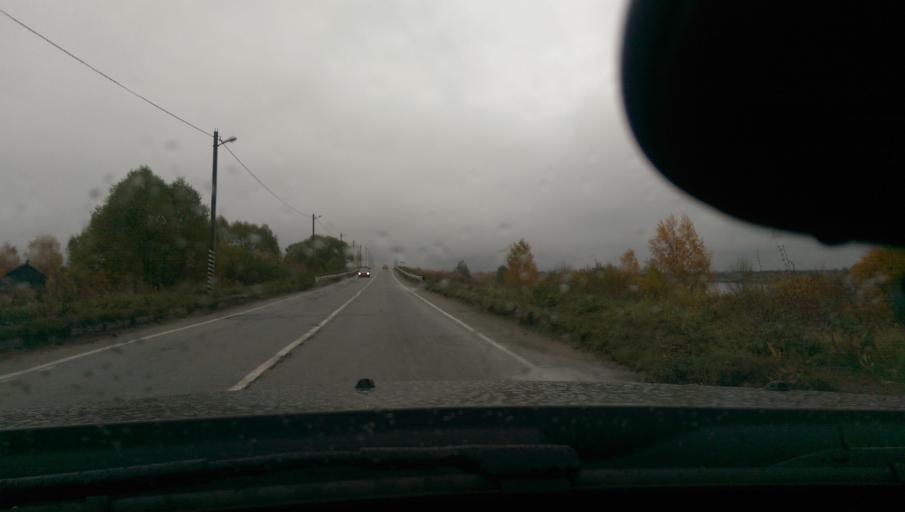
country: RU
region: Jaroslavl
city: Poshekhon'ye
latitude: 58.5106
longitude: 39.1163
